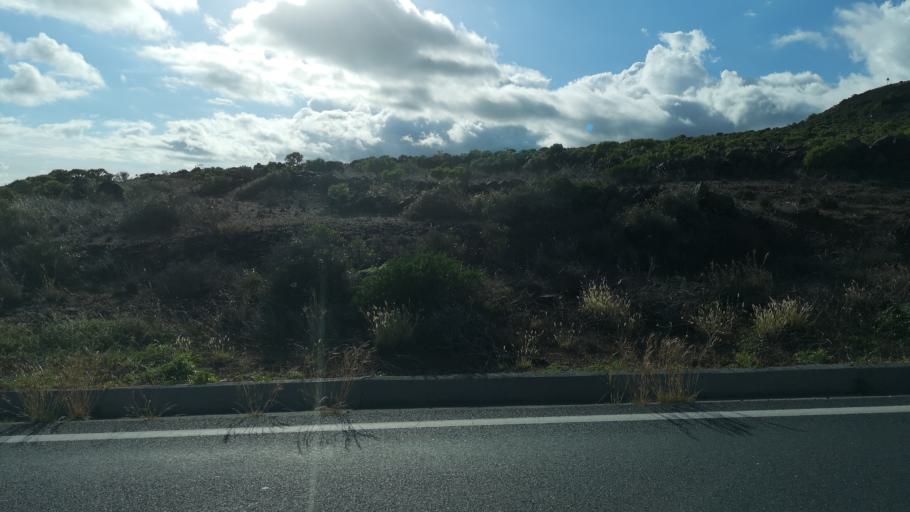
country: ES
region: Canary Islands
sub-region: Provincia de Santa Cruz de Tenerife
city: San Sebastian de la Gomera
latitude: 28.0846
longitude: -17.1413
